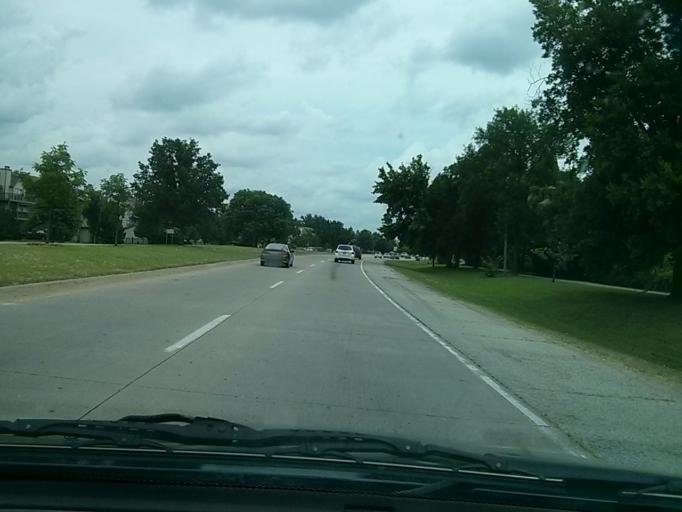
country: US
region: Oklahoma
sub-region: Tulsa County
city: Jenks
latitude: 36.0315
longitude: -95.9539
